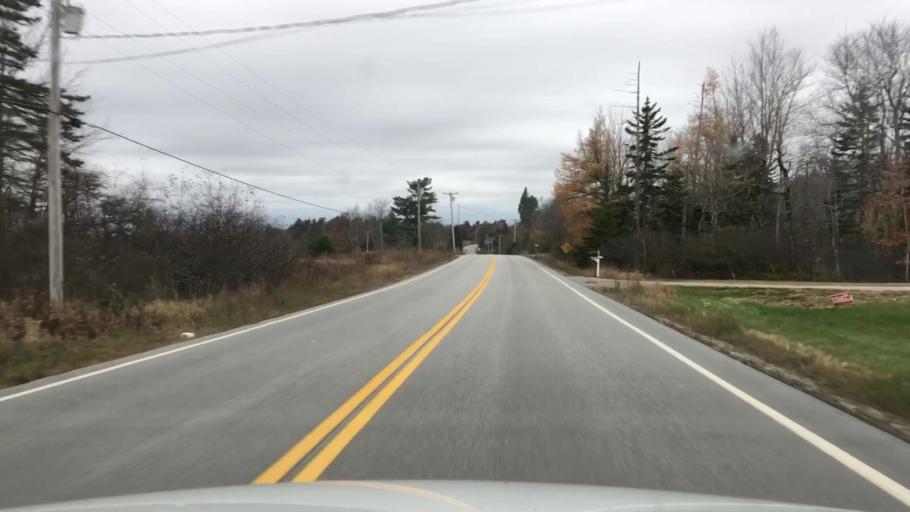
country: US
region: Maine
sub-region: Hancock County
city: Penobscot
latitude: 44.5278
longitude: -68.6680
